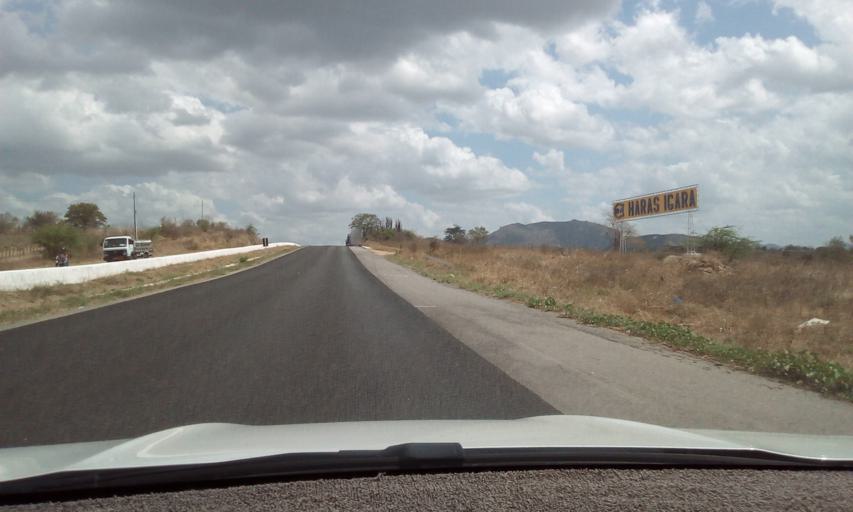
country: BR
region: Pernambuco
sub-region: Toritama
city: Toritama
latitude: -8.0467
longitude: -36.0504
